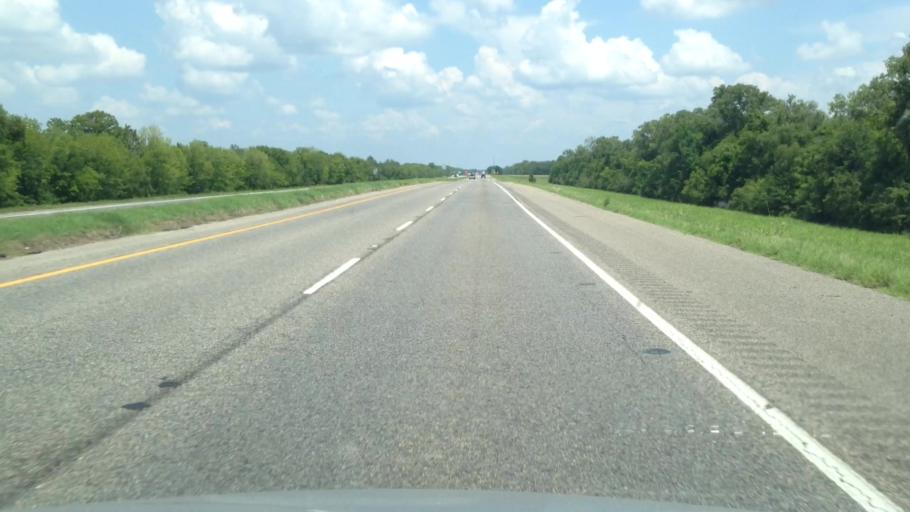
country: US
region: Louisiana
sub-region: Saint Landry Parish
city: Krotz Springs
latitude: 30.5469
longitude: -91.8209
